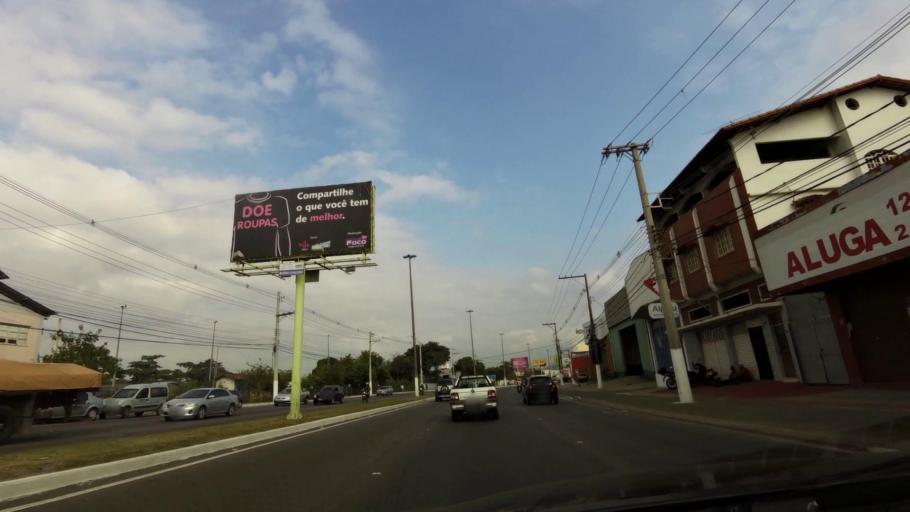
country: BR
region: Espirito Santo
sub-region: Vitoria
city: Vitoria
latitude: -20.3552
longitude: -40.3391
